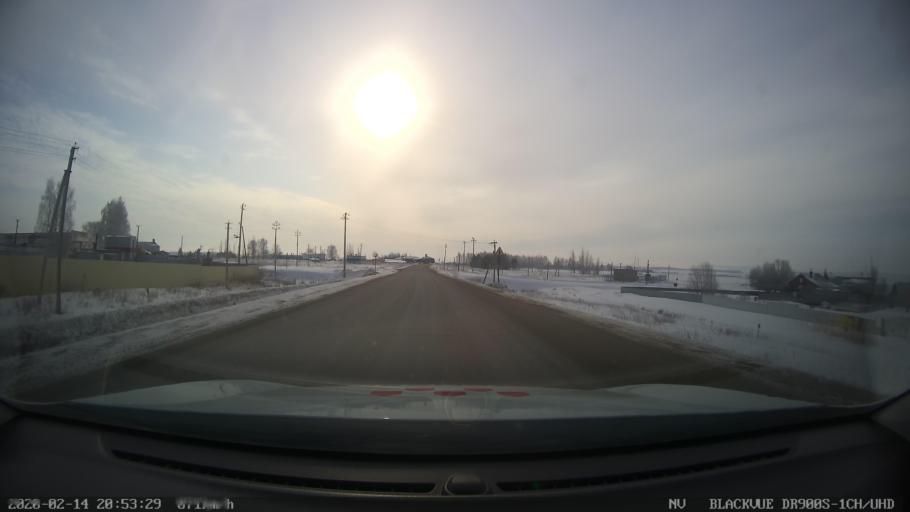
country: RU
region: Tatarstan
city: Kuybyshevskiy Zaton
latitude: 55.1940
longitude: 49.2473
